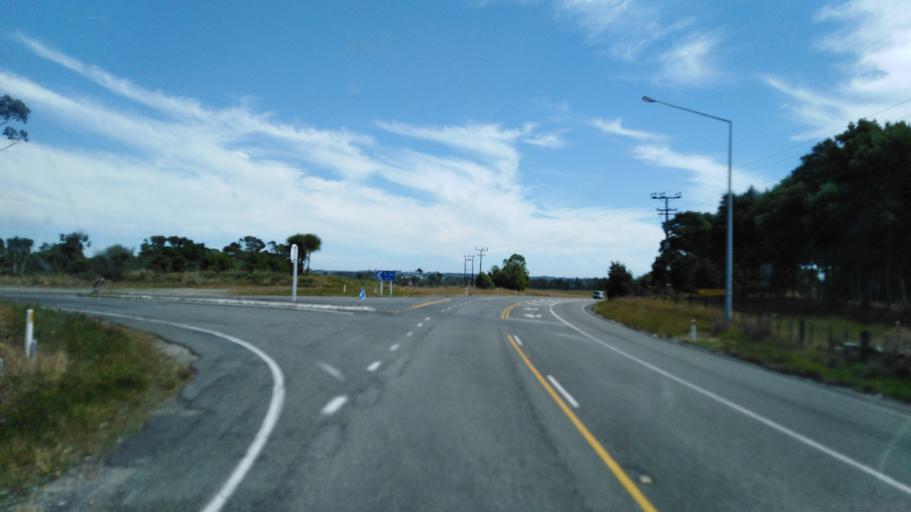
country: NZ
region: West Coast
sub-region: Buller District
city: Westport
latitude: -41.7595
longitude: 171.6471
